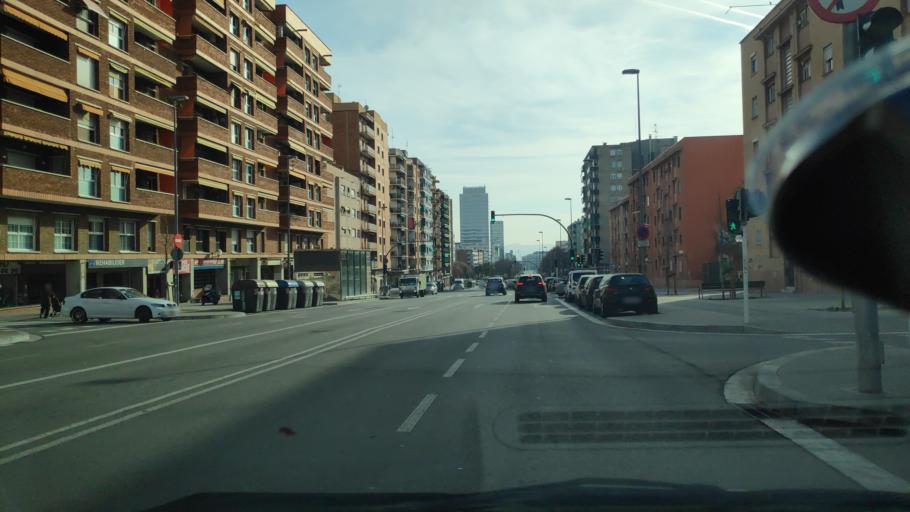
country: ES
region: Catalonia
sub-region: Provincia de Barcelona
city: Sabadell
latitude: 41.5610
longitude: 2.0967
